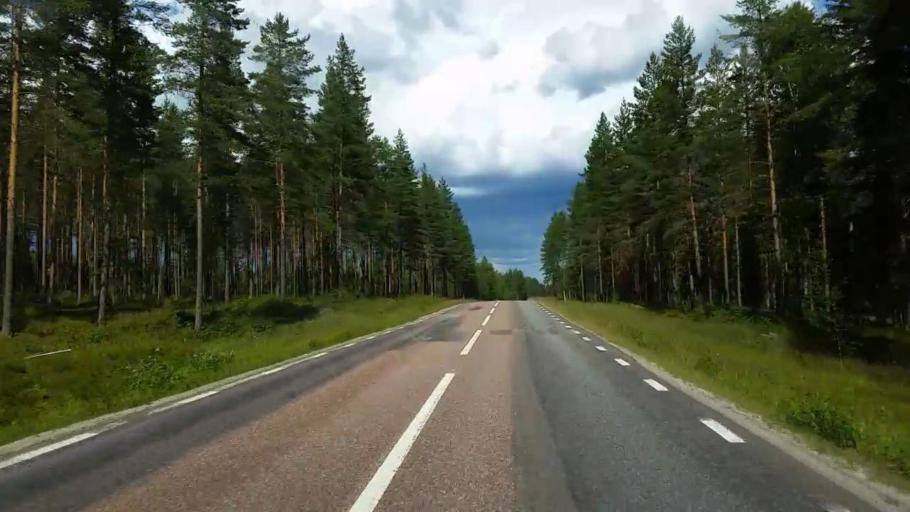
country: SE
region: Gaevleborg
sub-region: Ovanakers Kommun
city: Edsbyn
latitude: 61.3131
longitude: 15.5073
